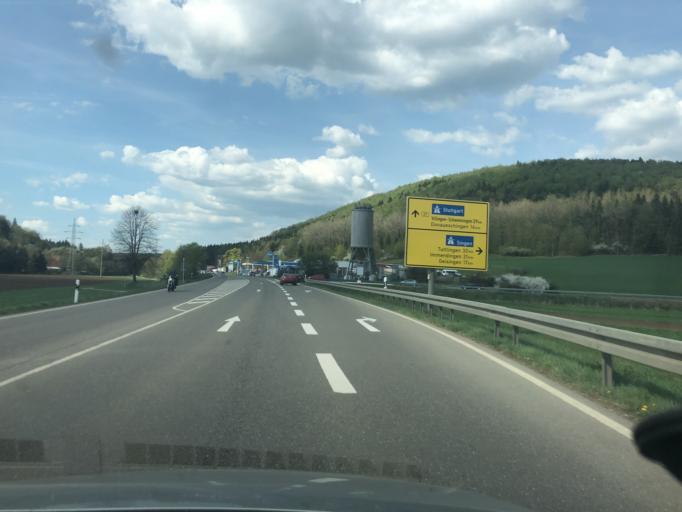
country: DE
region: Baden-Wuerttemberg
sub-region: Freiburg Region
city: Blumberg
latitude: 47.8438
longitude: 8.5551
